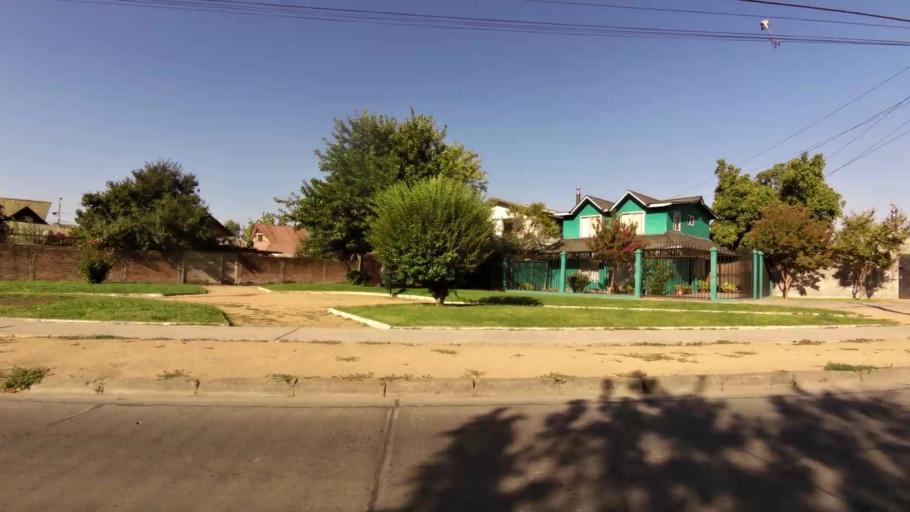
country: CL
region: Maule
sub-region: Provincia de Talca
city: Talca
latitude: -35.4419
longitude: -71.6689
